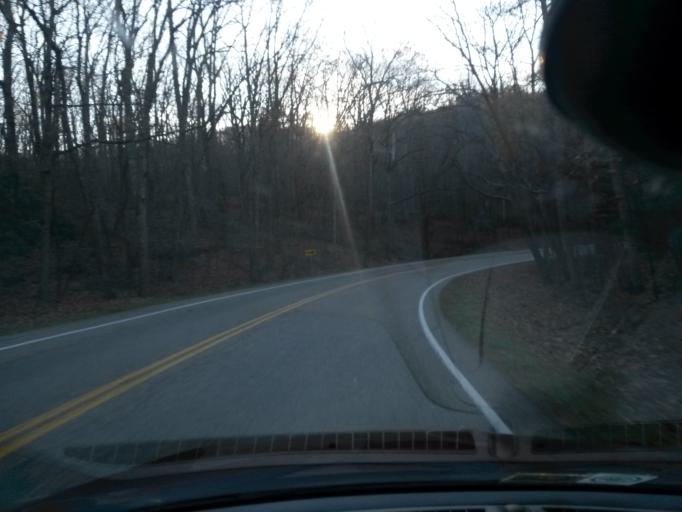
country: US
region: Virginia
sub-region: City of Buena Vista
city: Buena Vista
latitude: 37.7287
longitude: -79.3132
